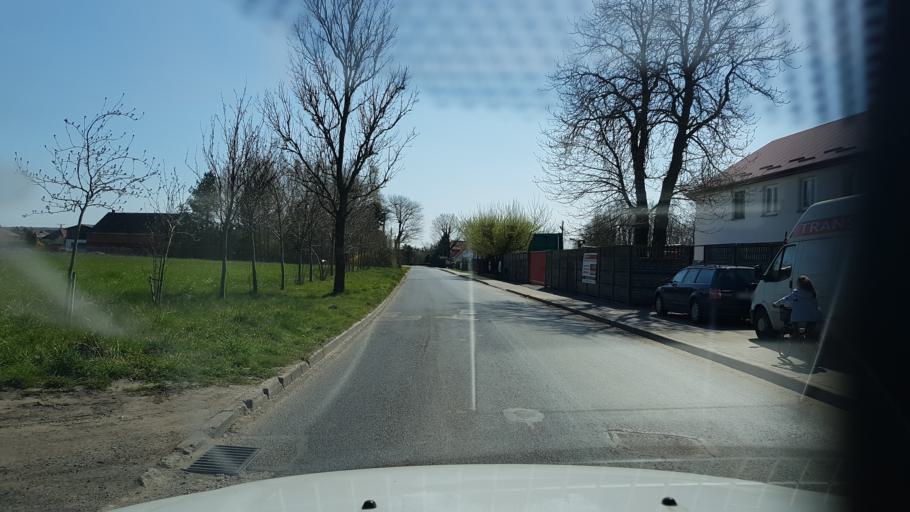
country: PL
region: West Pomeranian Voivodeship
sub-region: Koszalin
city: Koszalin
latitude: 54.2451
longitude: 16.1734
